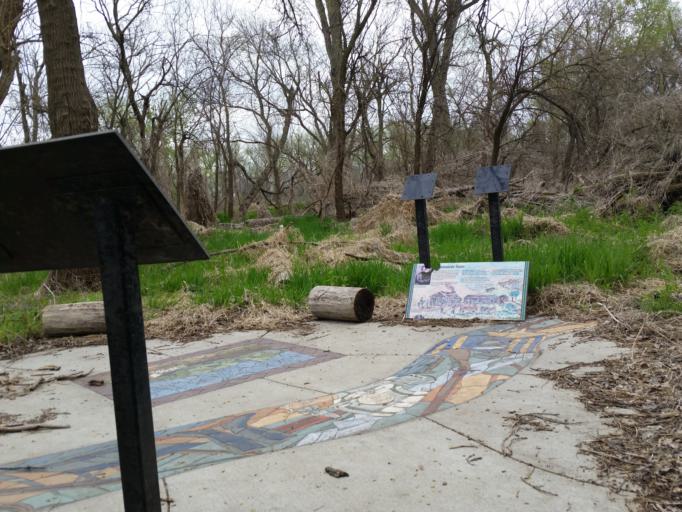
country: US
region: Nebraska
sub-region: Sarpy County
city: Bellevue
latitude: 41.1525
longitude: -95.8854
